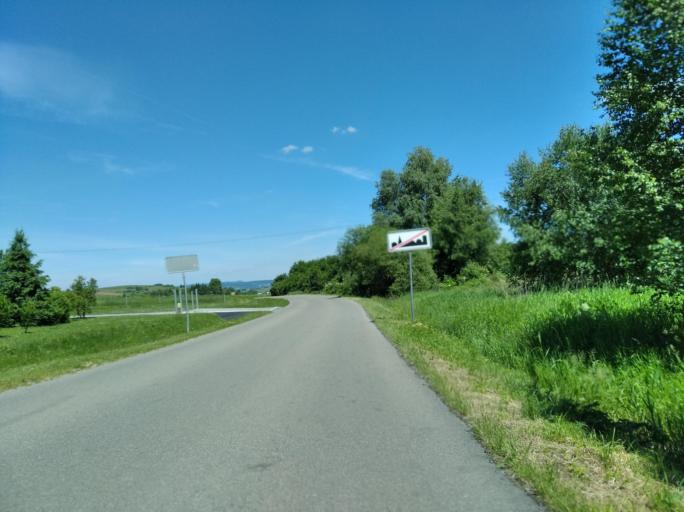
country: PL
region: Subcarpathian Voivodeship
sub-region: Powiat jasielski
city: Osiek Jasielski
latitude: 49.6745
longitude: 21.5421
